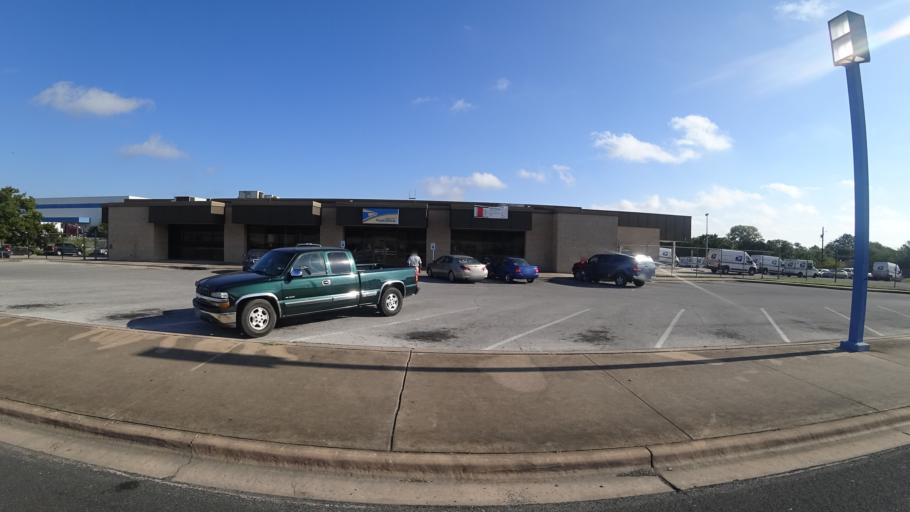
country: US
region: Texas
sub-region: Travis County
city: Austin
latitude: 30.3338
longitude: -97.6997
